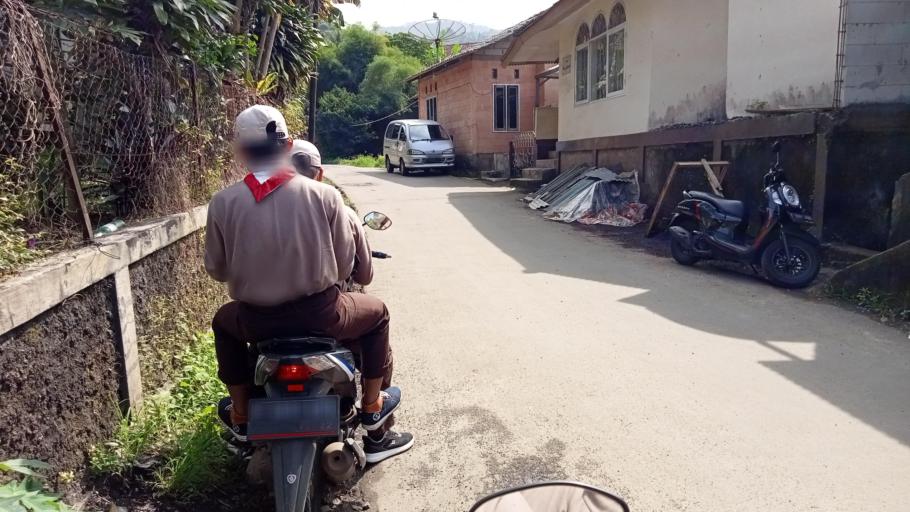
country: ID
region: West Java
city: Caringin
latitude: -6.6461
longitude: 106.9092
